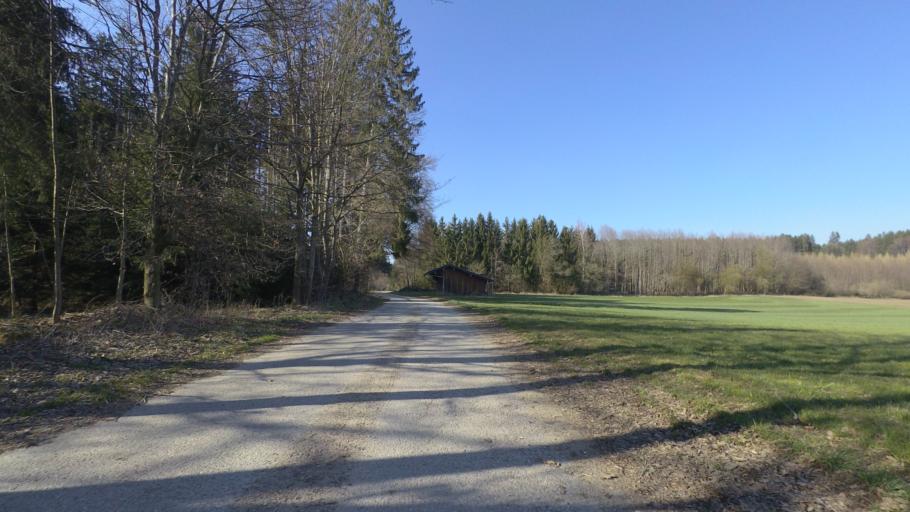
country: DE
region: Bavaria
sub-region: Upper Bavaria
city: Nussdorf
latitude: 47.8744
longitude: 12.5749
